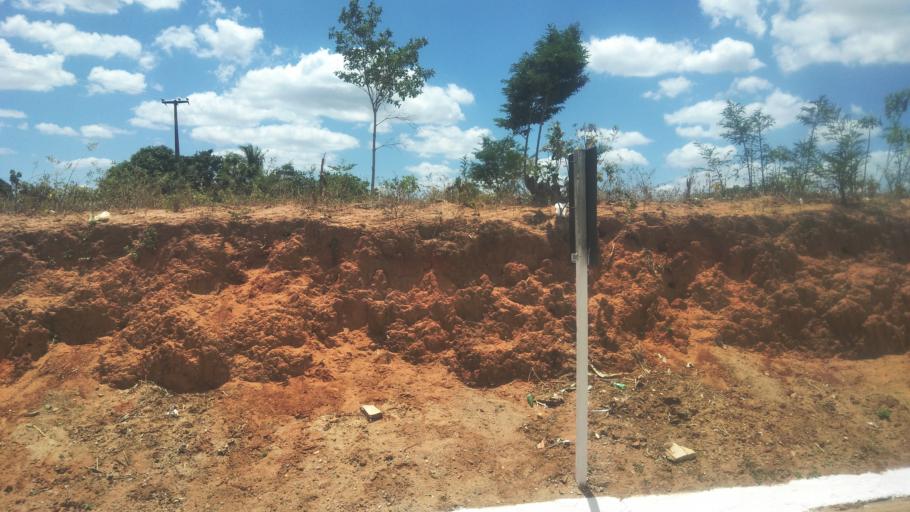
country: BR
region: Pernambuco
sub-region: Vicencia
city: Vicencia
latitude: -7.7285
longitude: -35.3236
